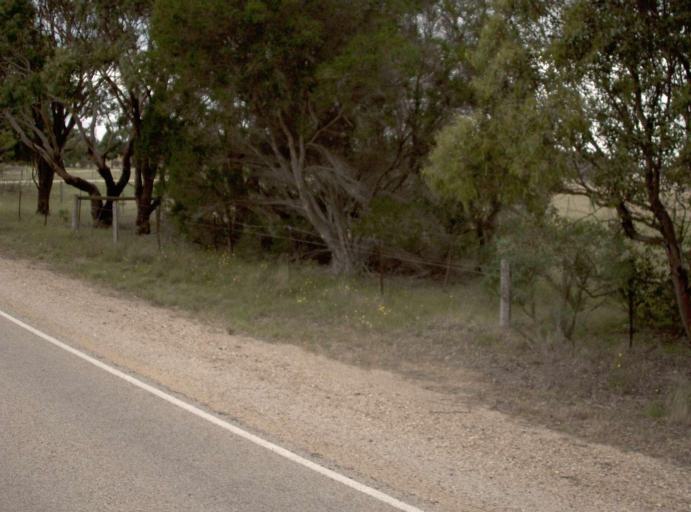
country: AU
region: Victoria
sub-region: East Gippsland
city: Bairnsdale
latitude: -37.8604
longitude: 147.5634
